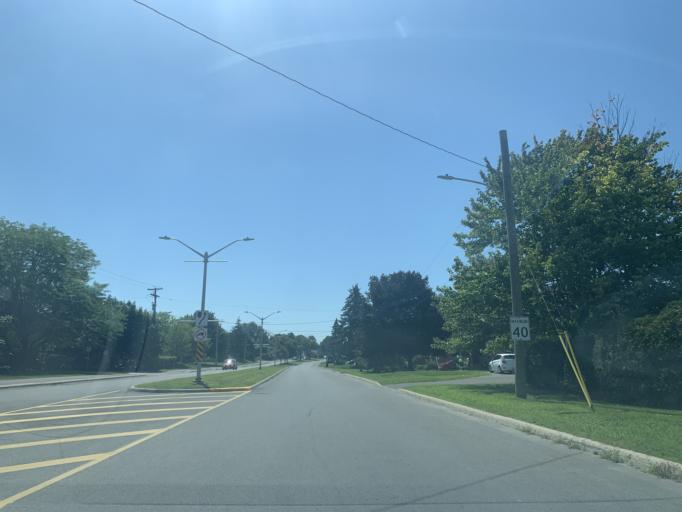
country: CA
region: Ontario
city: Hawkesbury
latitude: 45.6073
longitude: -74.6051
